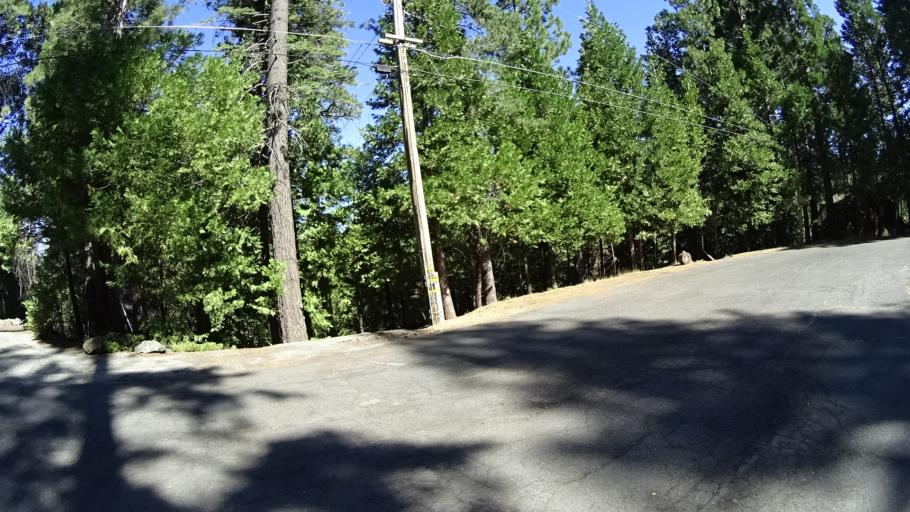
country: US
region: California
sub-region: Calaveras County
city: Arnold
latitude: 38.2480
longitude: -120.3268
